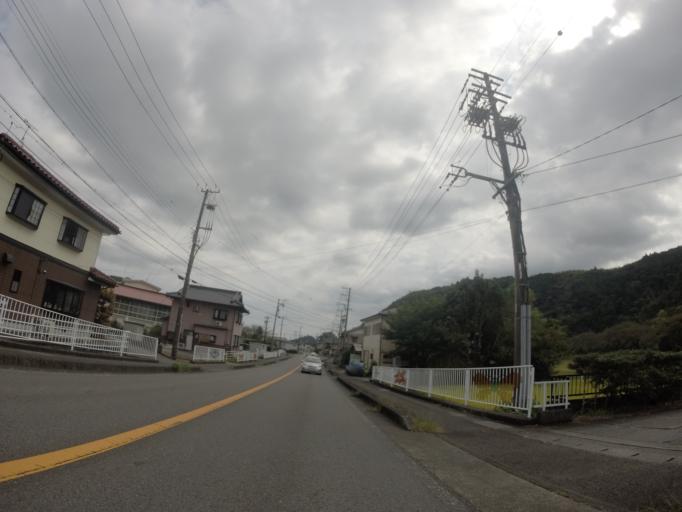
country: JP
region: Shizuoka
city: Fujieda
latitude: 34.8820
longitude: 138.2166
